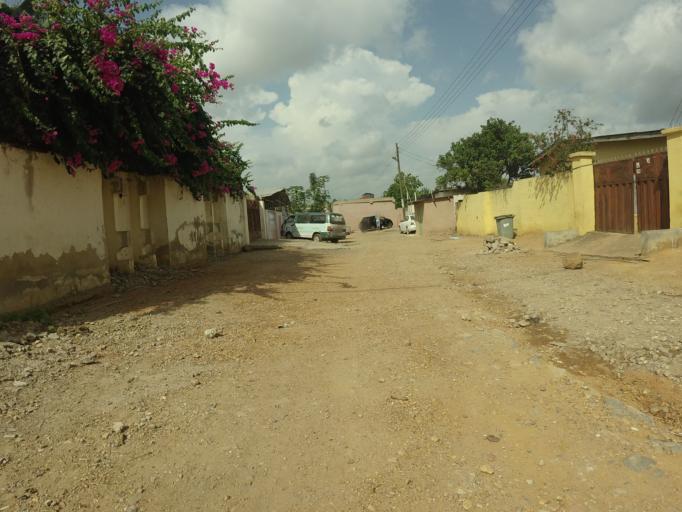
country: GH
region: Greater Accra
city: Dome
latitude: 5.6174
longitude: -0.2432
